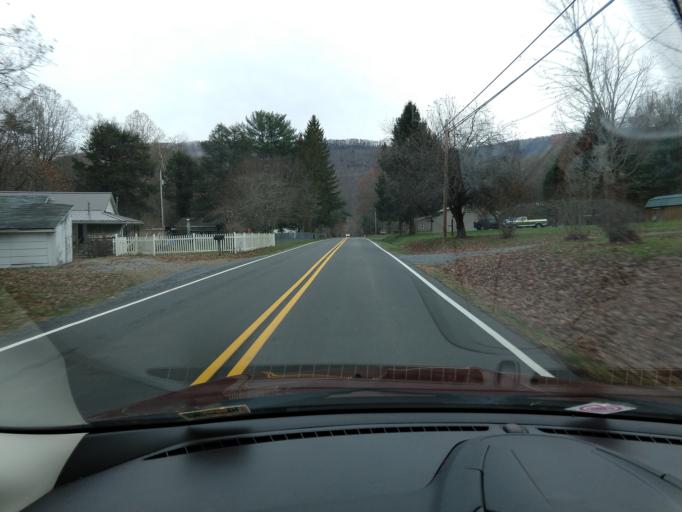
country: US
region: West Virginia
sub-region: Greenbrier County
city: White Sulphur Springs
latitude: 37.7239
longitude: -80.2101
